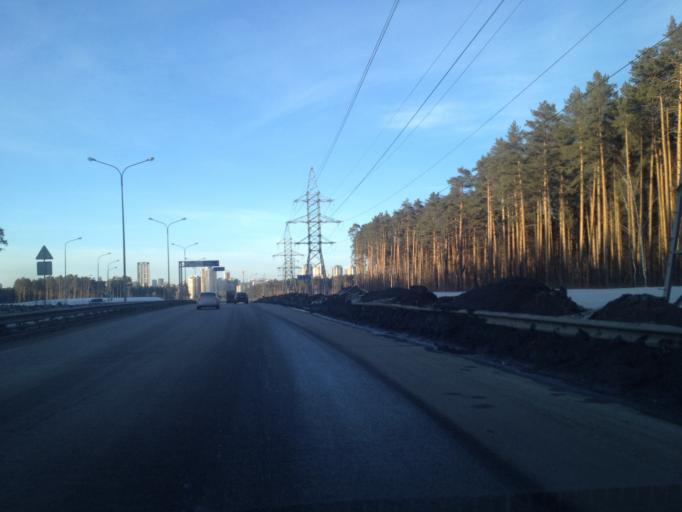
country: RU
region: Sverdlovsk
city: Sovkhoznyy
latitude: 56.7854
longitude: 60.5982
